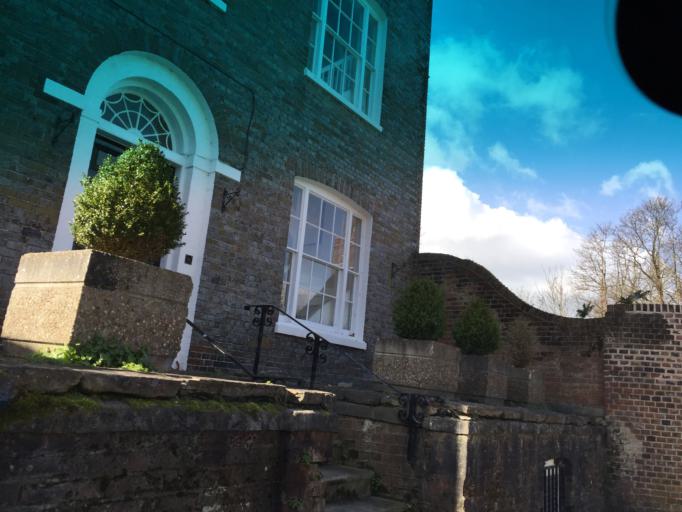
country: GB
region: England
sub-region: Hampshire
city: Gosport
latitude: 50.7926
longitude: -1.1192
